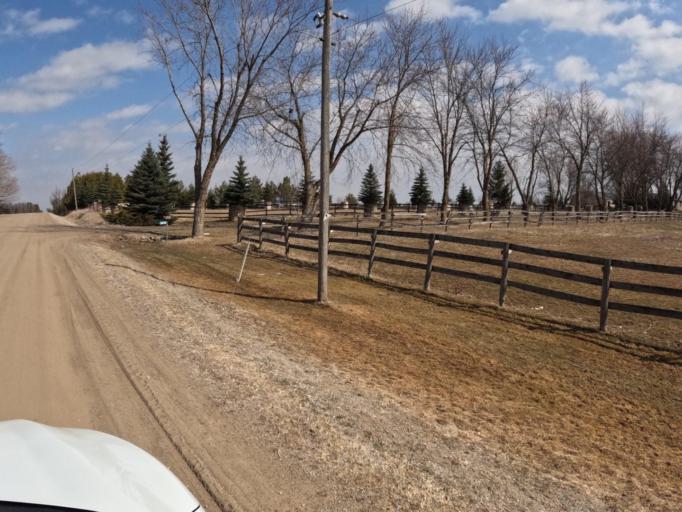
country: CA
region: Ontario
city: Orangeville
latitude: 43.9018
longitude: -80.2511
